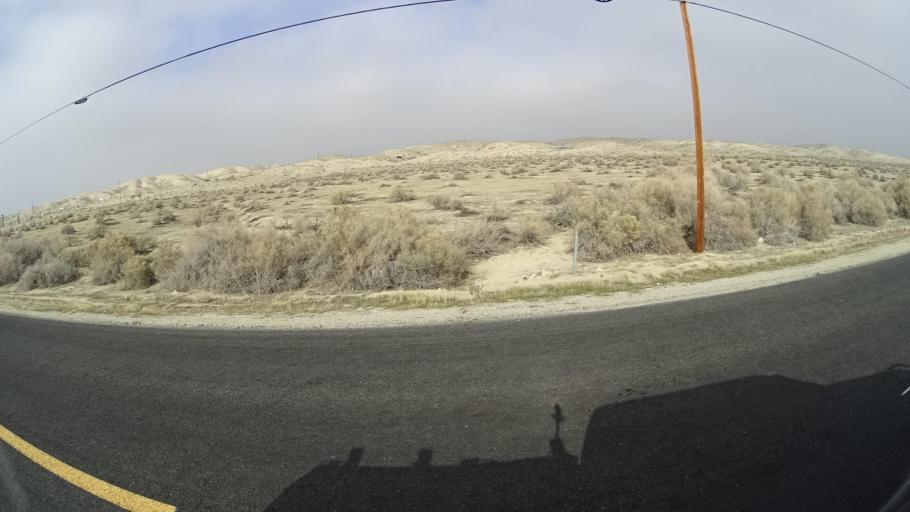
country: US
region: California
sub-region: Kern County
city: Ford City
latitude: 35.2322
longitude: -119.3648
